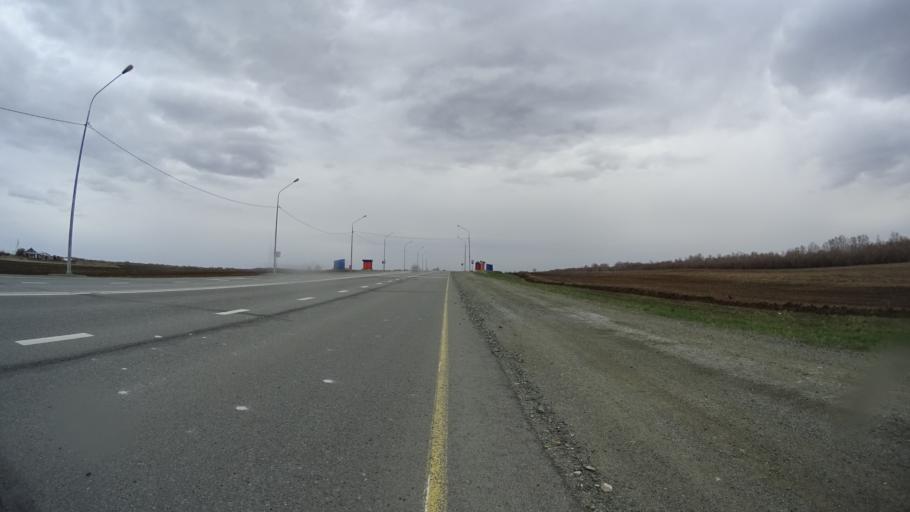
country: RU
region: Chelyabinsk
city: Krasnogorskiy
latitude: 54.6730
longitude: 61.2495
